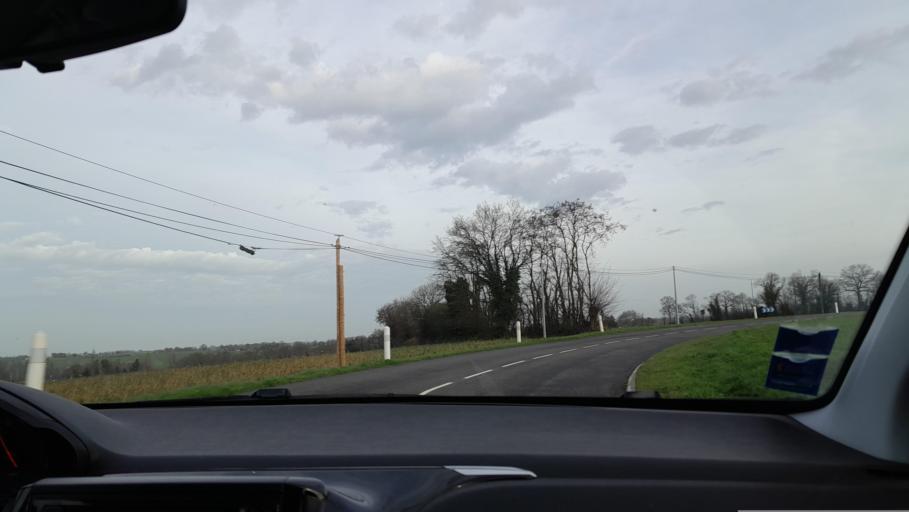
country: FR
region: Brittany
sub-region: Departement d'Ille-et-Vilaine
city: La Guerche-de-Bretagne
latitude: 47.9557
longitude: -1.1771
